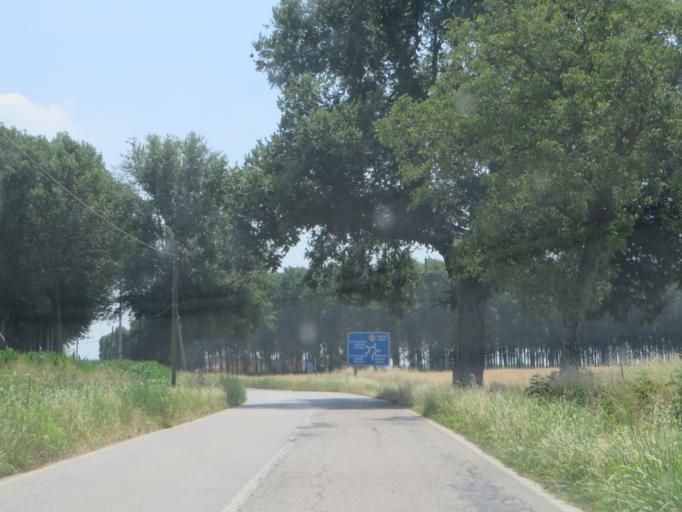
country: IT
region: Veneto
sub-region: Provincia di Verona
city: San Pietro di Morubio
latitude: 45.2309
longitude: 11.2313
